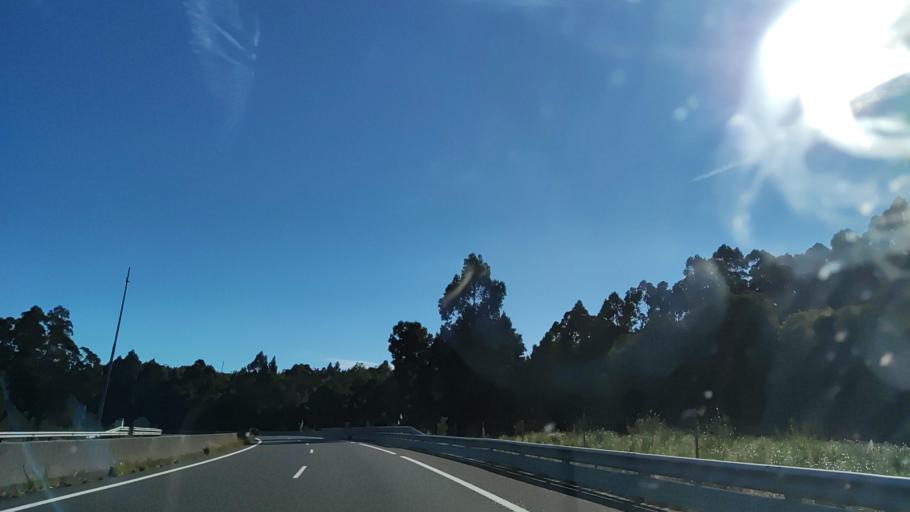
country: ES
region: Galicia
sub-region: Provincia da Coruna
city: Boiro
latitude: 42.6050
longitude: -8.9690
